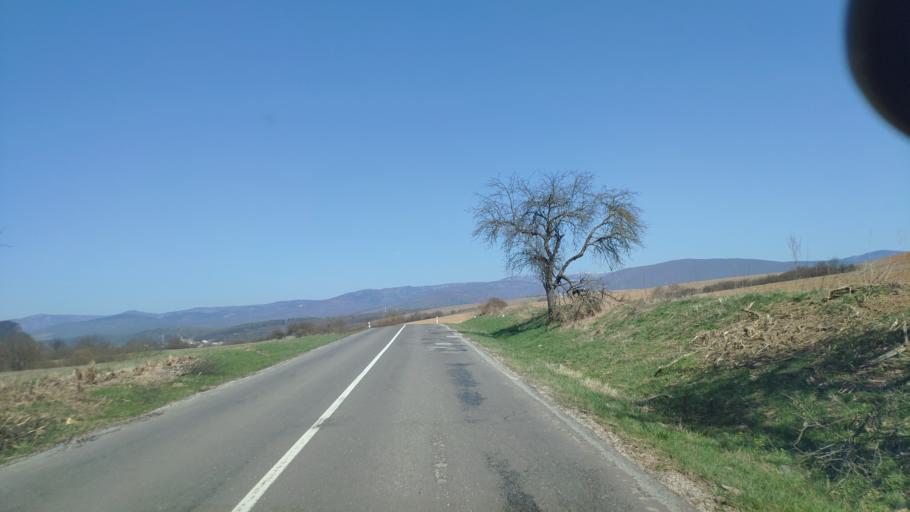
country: SK
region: Kosicky
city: Moldava nad Bodvou
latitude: 48.6633
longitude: 20.9980
